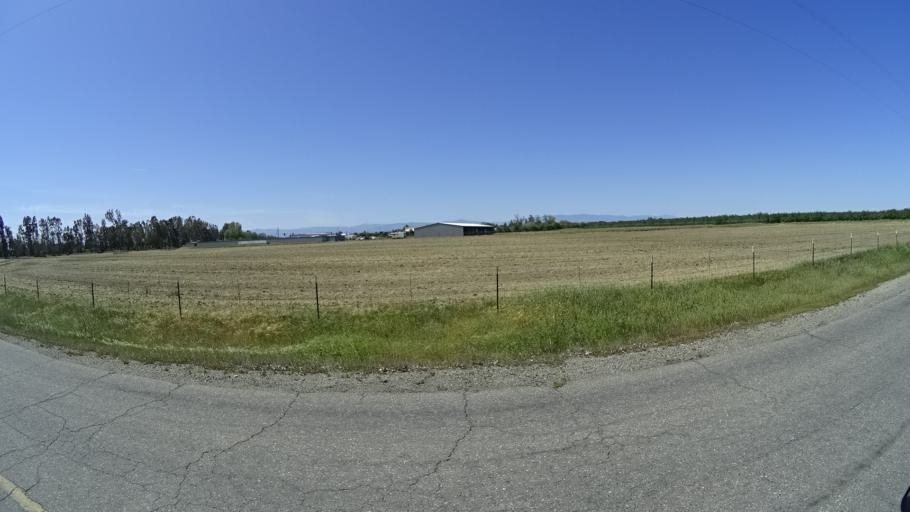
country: US
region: California
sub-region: Glenn County
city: Orland
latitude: 39.7348
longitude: -122.1591
